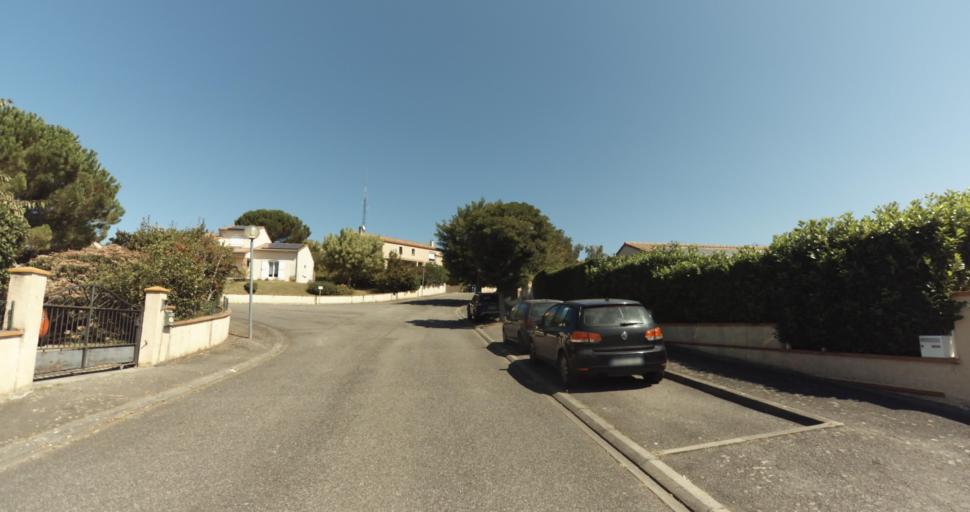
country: FR
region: Midi-Pyrenees
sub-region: Departement de la Haute-Garonne
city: L'Union
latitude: 43.6502
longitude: 1.4931
